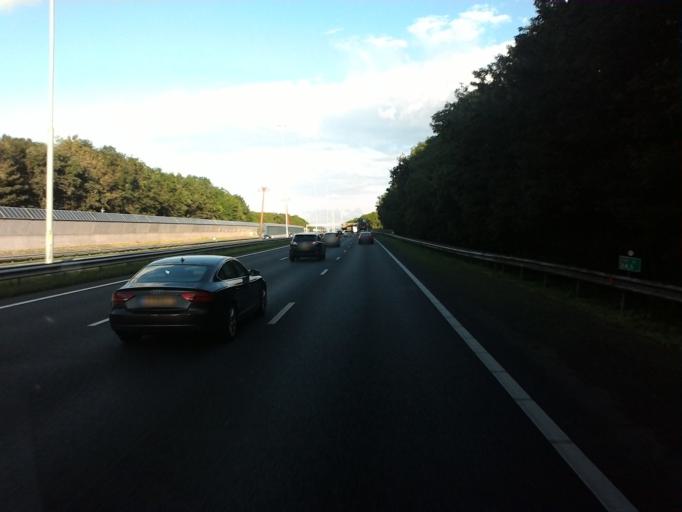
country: NL
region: North Holland
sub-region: Gemeente Ouder-Amstel
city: Ouderkerk aan de Amstel
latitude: 52.2888
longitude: 4.9121
